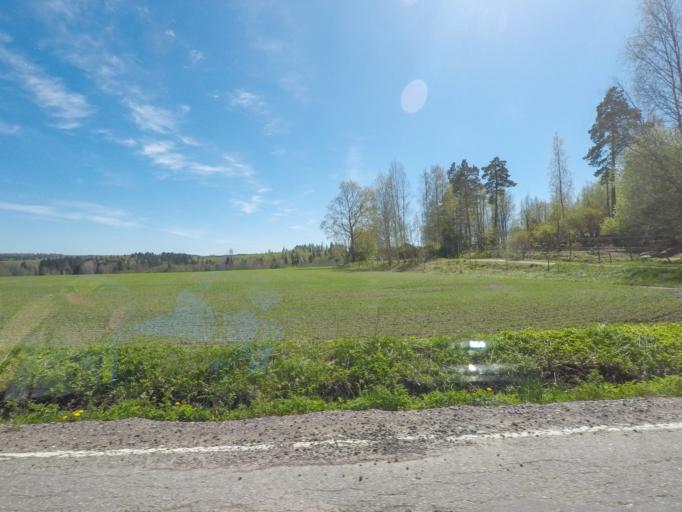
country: FI
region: Uusimaa
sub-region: Helsinki
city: Sammatti
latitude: 60.4710
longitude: 23.8288
